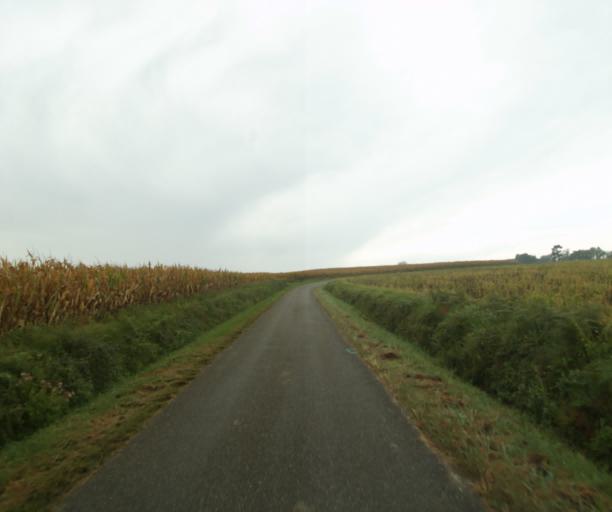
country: FR
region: Midi-Pyrenees
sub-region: Departement du Gers
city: Cazaubon
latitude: 43.9240
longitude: -0.0899
